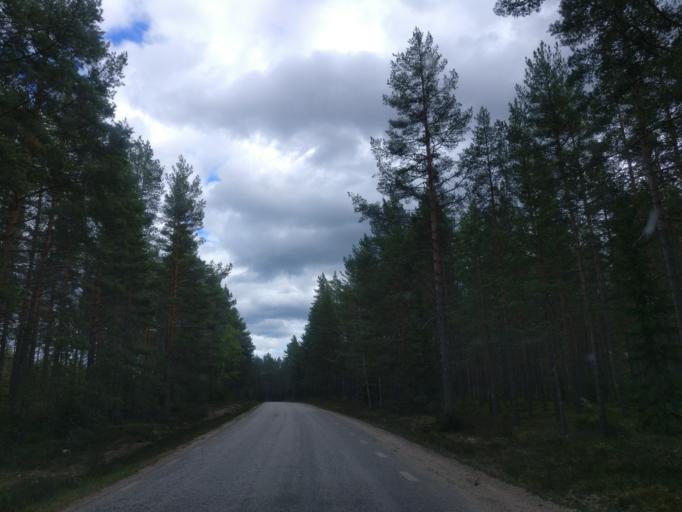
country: SE
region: Gaevleborg
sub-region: Soderhamns Kommun
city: Marielund
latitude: 61.4650
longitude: 17.0836
